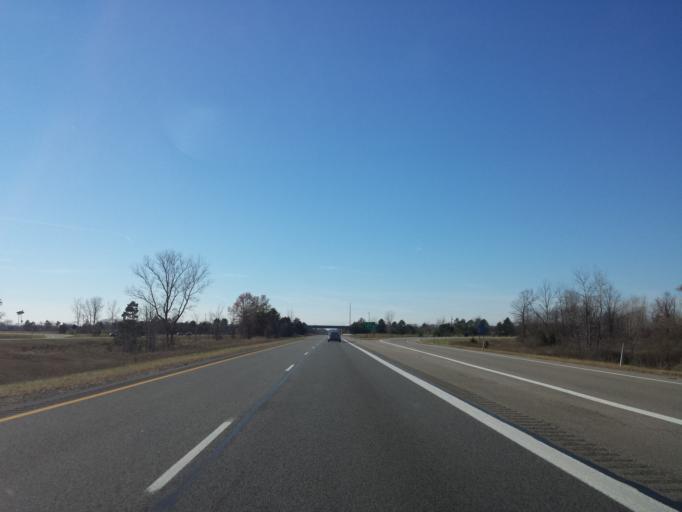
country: US
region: Michigan
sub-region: Ingham County
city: Williamston
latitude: 42.6657
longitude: -84.2760
